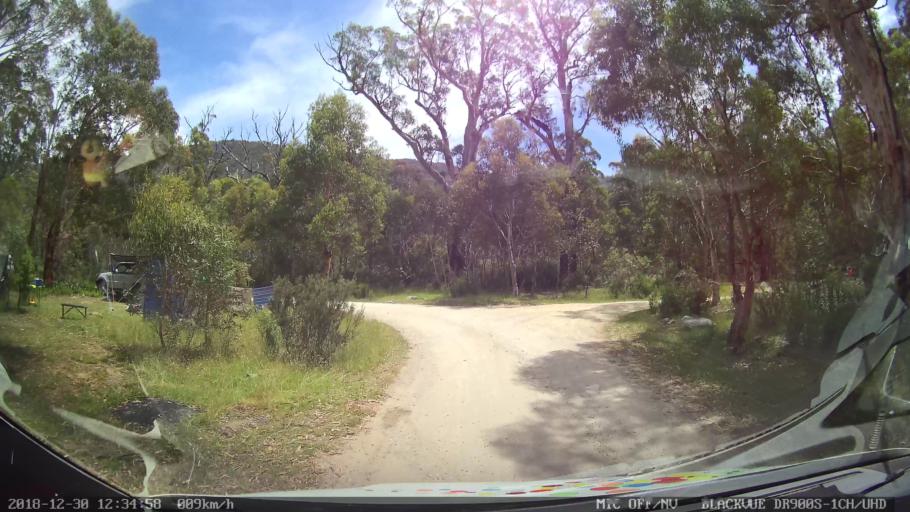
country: AU
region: New South Wales
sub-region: Snowy River
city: Jindabyne
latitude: -36.3214
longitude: 148.4653
